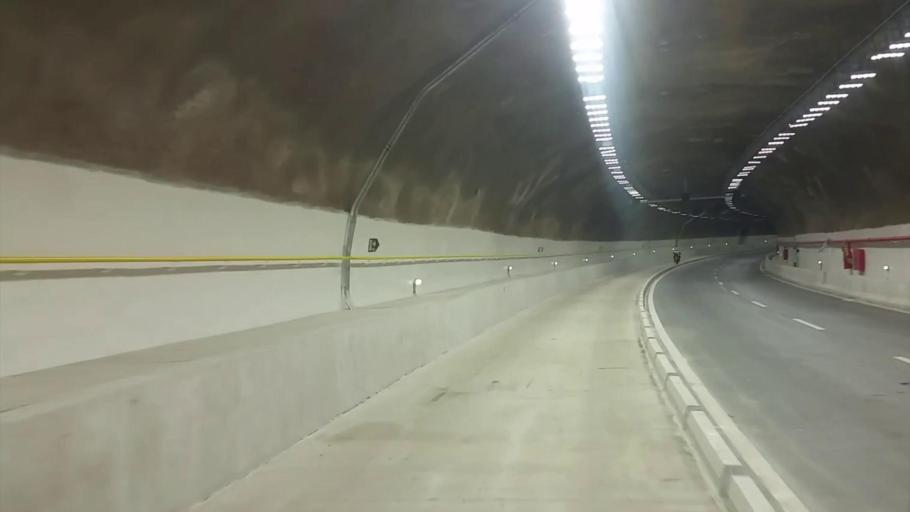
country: BR
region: Rio de Janeiro
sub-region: Nilopolis
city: Nilopolis
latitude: -22.8995
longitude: -43.3980
